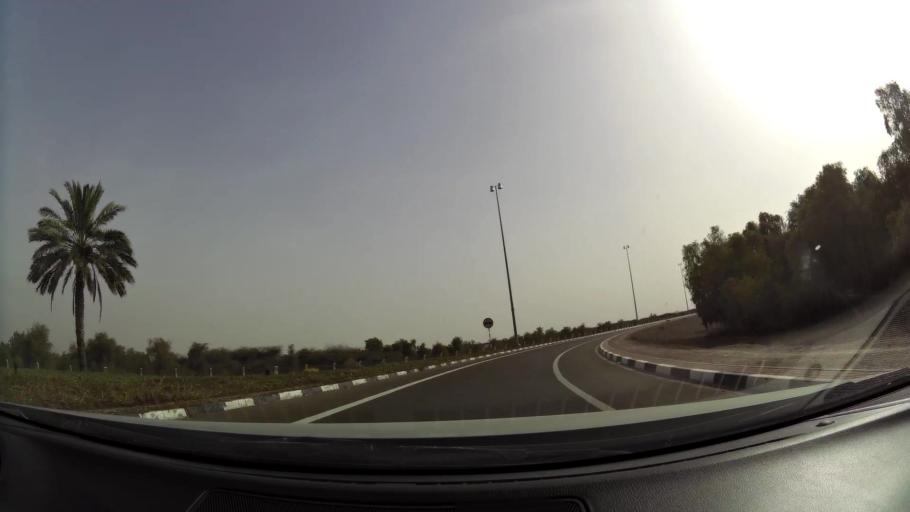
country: AE
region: Abu Dhabi
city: Al Ain
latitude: 24.1820
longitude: 55.5971
